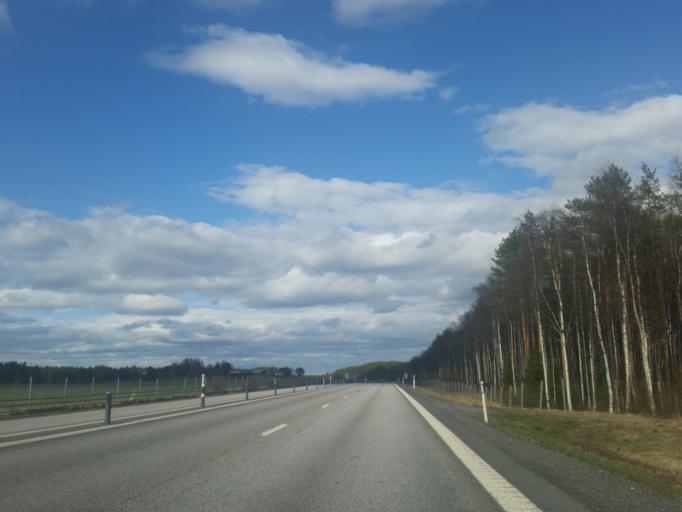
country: SE
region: Vaesterbotten
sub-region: Robertsfors Kommun
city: Robertsfors
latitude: 64.1486
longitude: 20.9043
